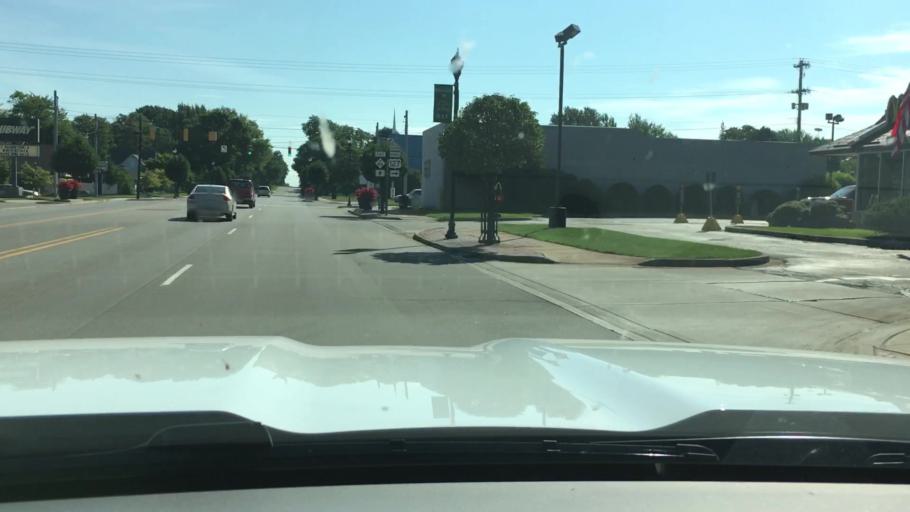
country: US
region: Michigan
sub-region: Gratiot County
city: Saint Louis
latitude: 43.4079
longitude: -84.6083
